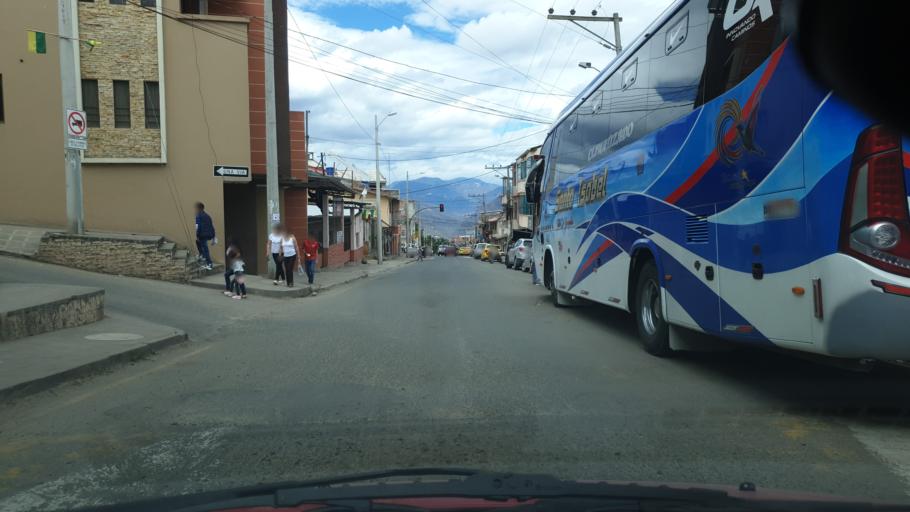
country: EC
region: Azuay
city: Cuenca
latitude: -3.2749
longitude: -79.3160
